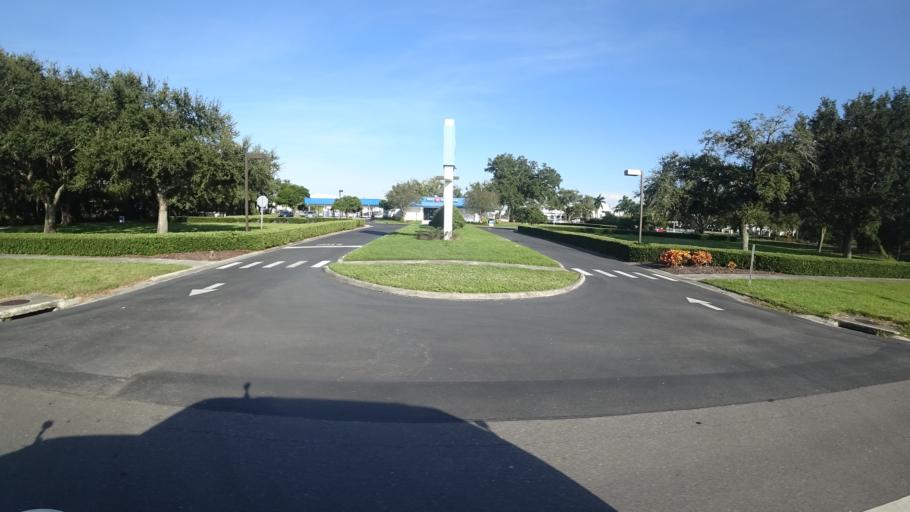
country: US
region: Florida
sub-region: Manatee County
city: Whitfield
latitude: 27.4194
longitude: -82.5467
